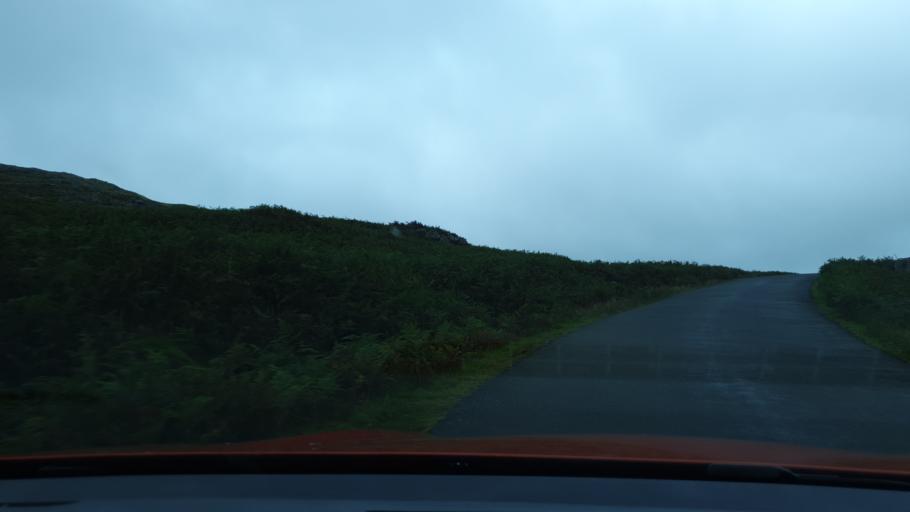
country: GB
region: England
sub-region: Cumbria
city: Millom
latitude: 54.3802
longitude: -3.2910
